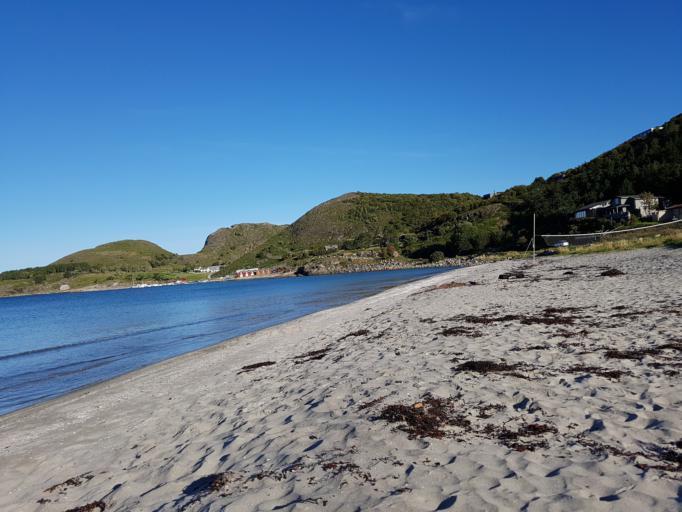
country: NO
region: Sor-Trondelag
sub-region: Afjord
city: A i Afjord
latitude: 64.0538
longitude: 9.9502
